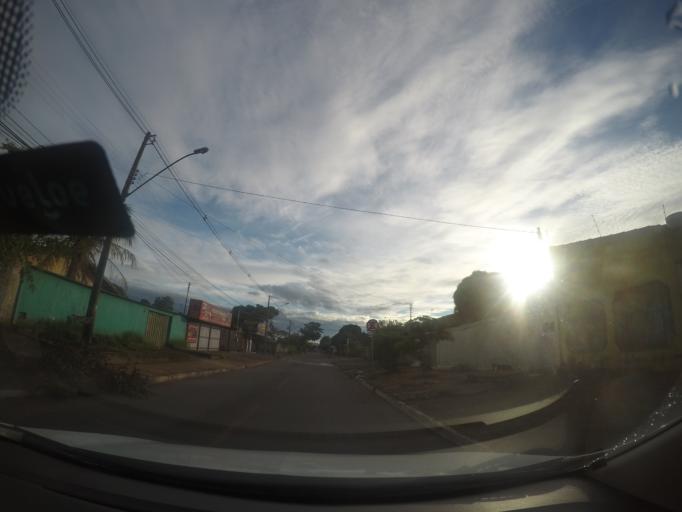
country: BR
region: Goias
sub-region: Goiania
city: Goiania
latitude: -16.6490
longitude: -49.3340
